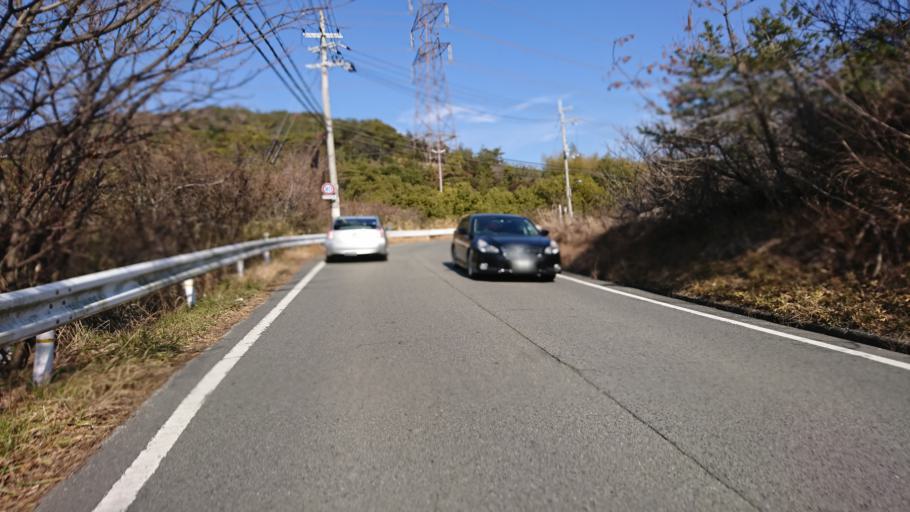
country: JP
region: Hyogo
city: Kakogawacho-honmachi
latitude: 34.7971
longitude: 134.8397
